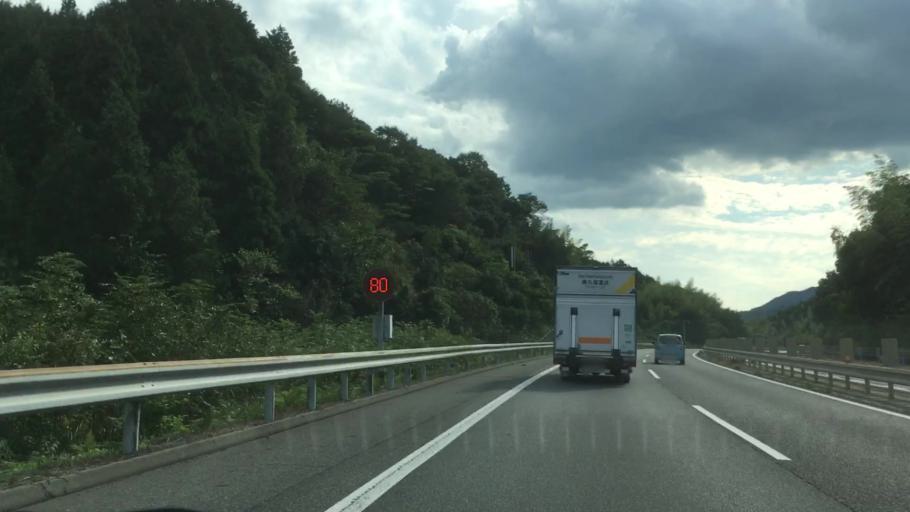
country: JP
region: Yamaguchi
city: Iwakuni
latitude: 34.1442
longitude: 132.1244
